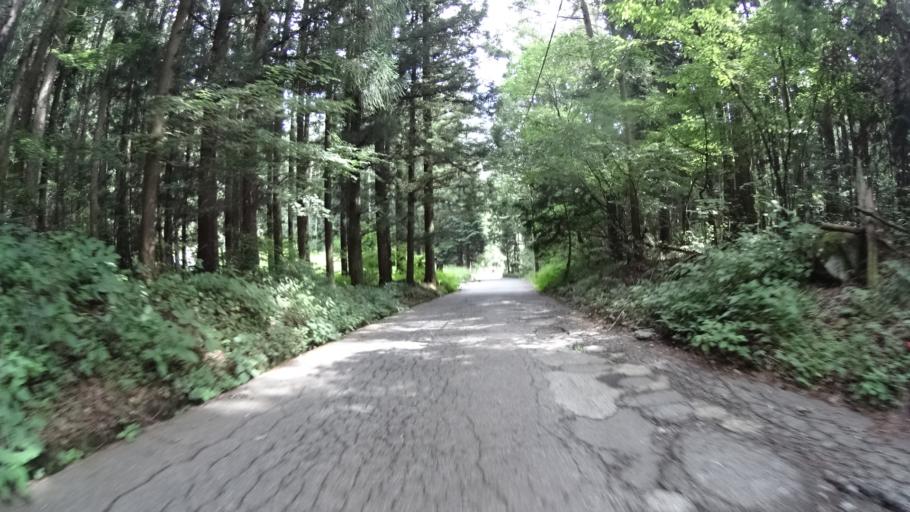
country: JP
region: Yamanashi
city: Nirasaki
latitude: 35.7877
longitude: 138.5322
